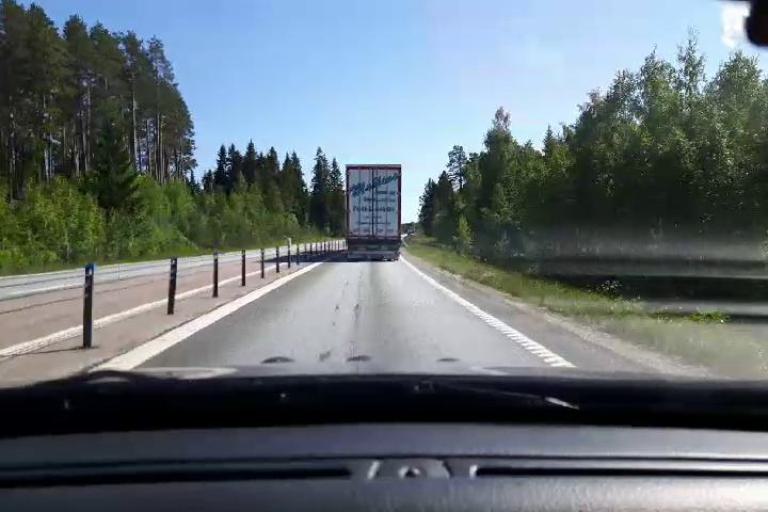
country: SE
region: Gaevleborg
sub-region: Soderhamns Kommun
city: Soderhamn
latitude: 61.2565
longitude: 17.0350
